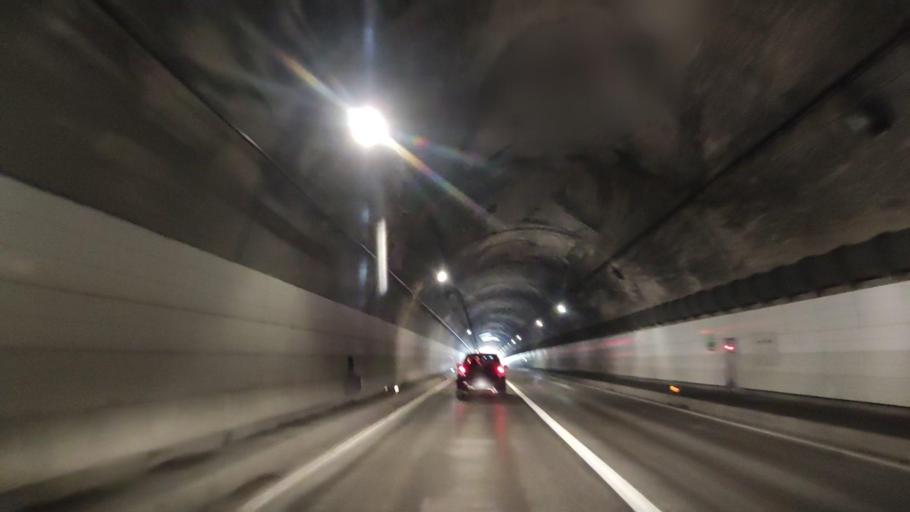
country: JP
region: Akita
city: Takanosu
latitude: 40.2125
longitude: 140.2173
